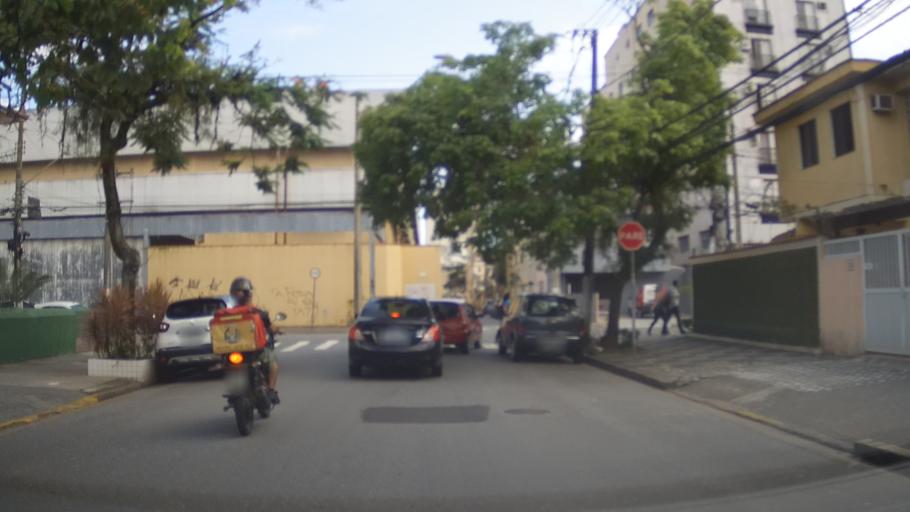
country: BR
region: Sao Paulo
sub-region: Santos
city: Santos
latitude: -23.9571
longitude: -46.3352
